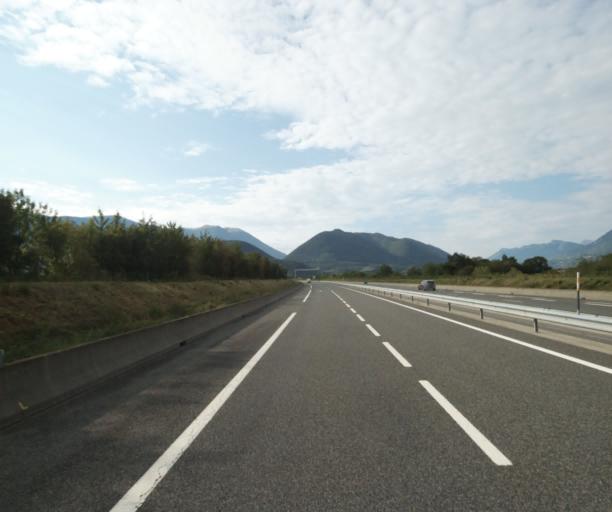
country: FR
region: Rhone-Alpes
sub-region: Departement de l'Isere
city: Vif
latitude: 45.0719
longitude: 5.6799
